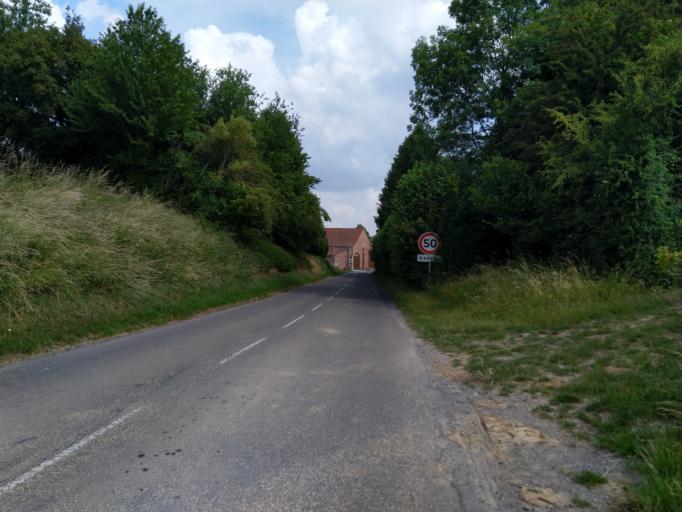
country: FR
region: Nord-Pas-de-Calais
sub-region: Departement du Nord
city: Rousies
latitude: 50.3188
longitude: 4.0040
